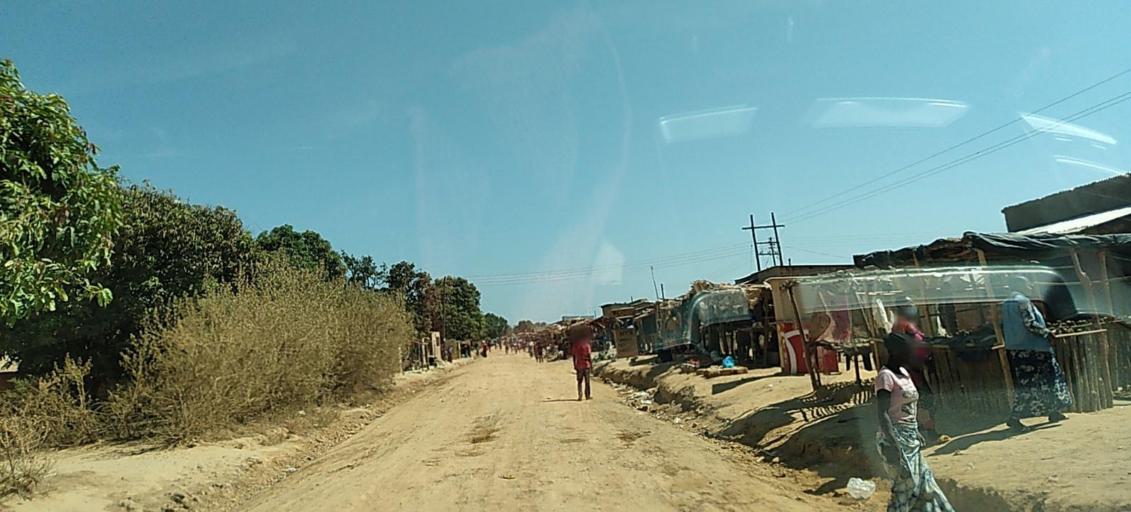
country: ZM
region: Copperbelt
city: Chililabombwe
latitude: -12.3282
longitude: 27.8603
